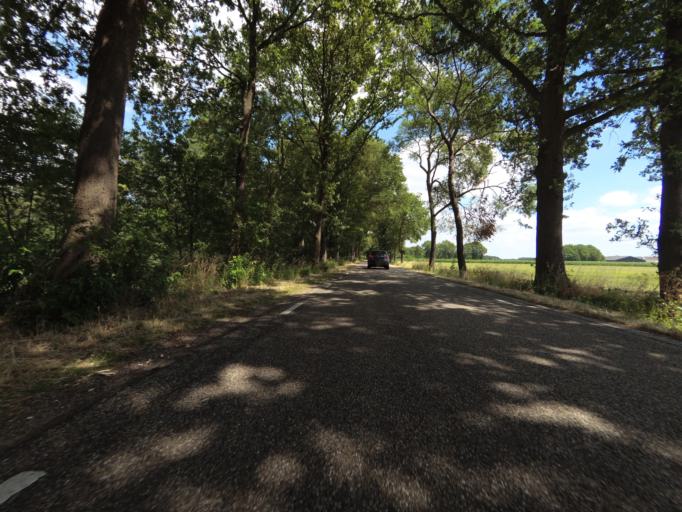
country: NL
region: Overijssel
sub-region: Gemeente Raalte
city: Raalte
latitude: 52.3050
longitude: 6.2860
